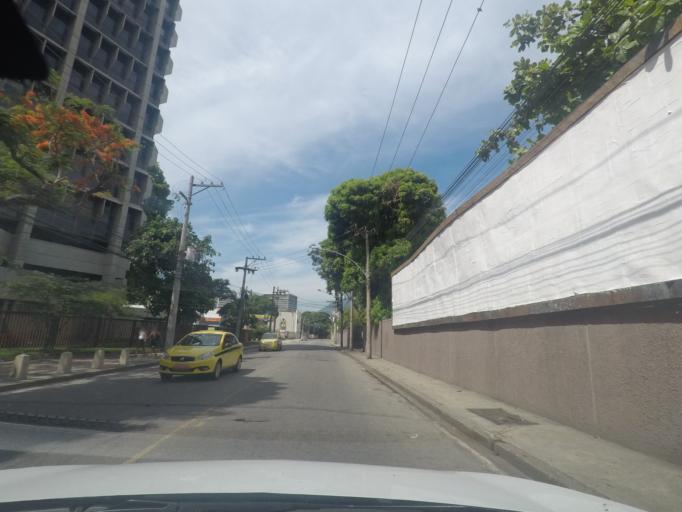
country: BR
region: Rio de Janeiro
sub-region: Rio De Janeiro
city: Rio de Janeiro
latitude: -22.9077
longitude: -43.2194
